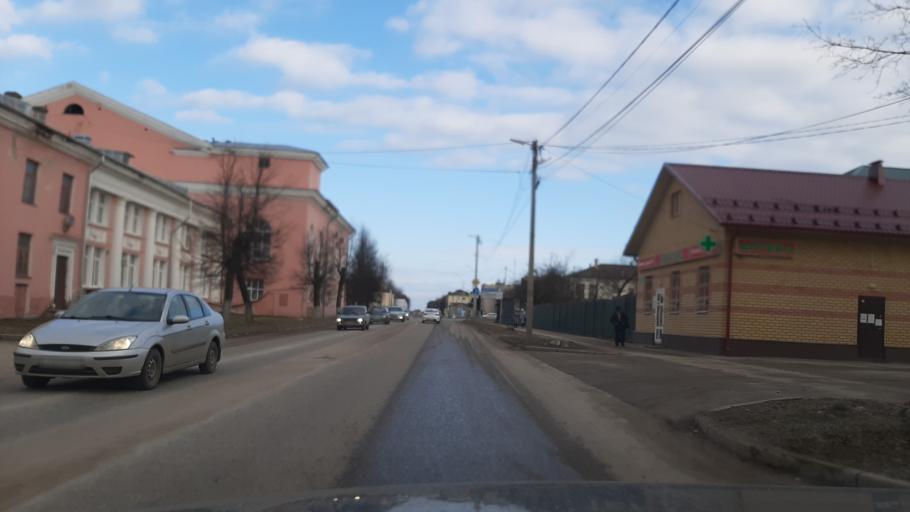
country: RU
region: Ivanovo
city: Teykovo
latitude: 56.8543
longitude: 40.5321
